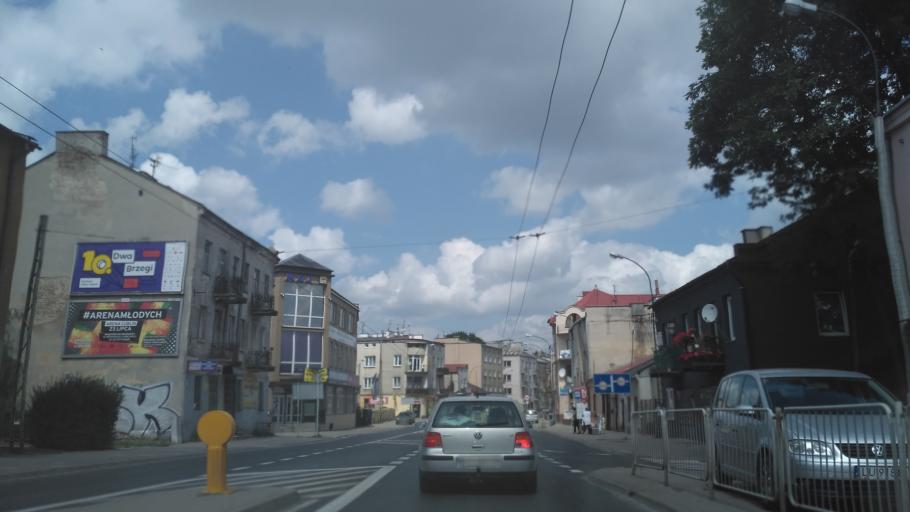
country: PL
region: Lublin Voivodeship
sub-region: Powiat lubelski
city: Lublin
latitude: 51.2252
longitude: 22.5740
